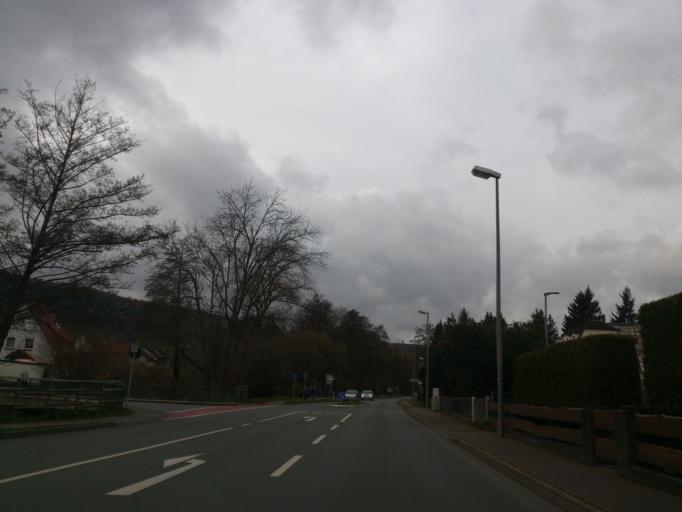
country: DE
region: North Rhine-Westphalia
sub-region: Regierungsbezirk Detmold
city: Hoexter
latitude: 51.7739
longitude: 9.3584
